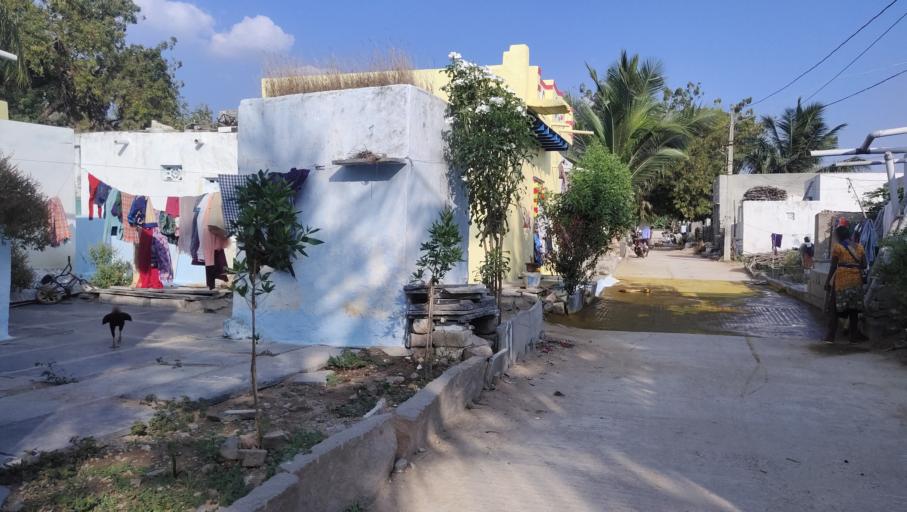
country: IN
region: Andhra Pradesh
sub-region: Anantapur
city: Tadpatri
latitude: 14.9322
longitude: 77.8645
